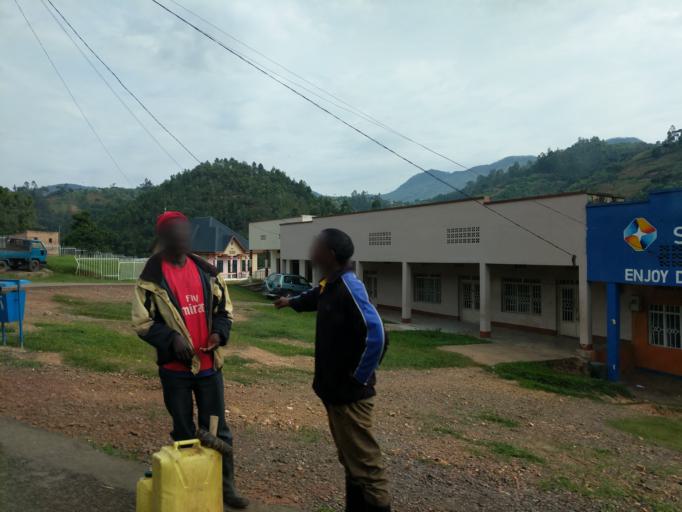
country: RW
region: Northern Province
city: Musanze
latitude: -1.6482
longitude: 29.7933
